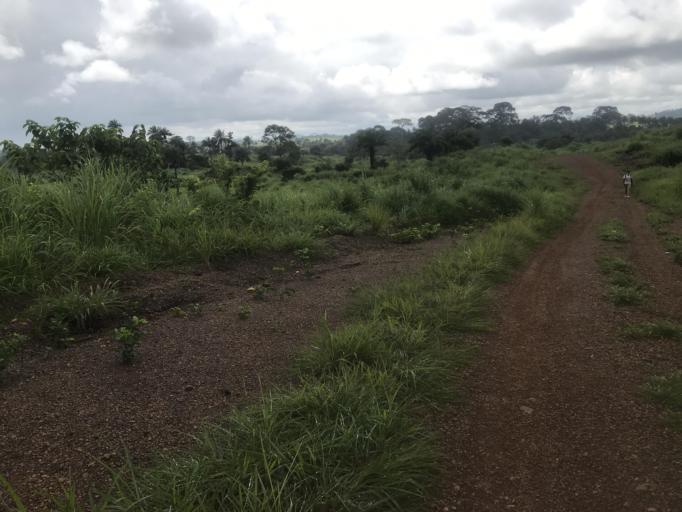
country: GN
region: Nzerekore
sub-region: Prefecture de Guekedou
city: Gueckedou
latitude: 8.4757
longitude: -10.2901
